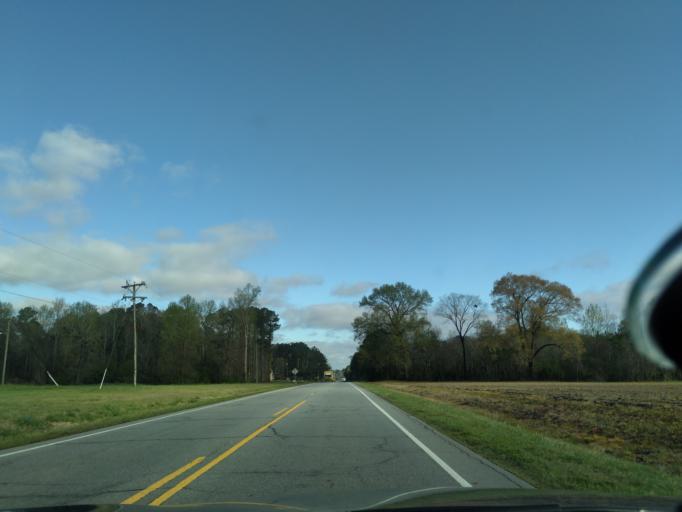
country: US
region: North Carolina
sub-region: Washington County
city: Plymouth
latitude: 36.0174
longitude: -76.7787
